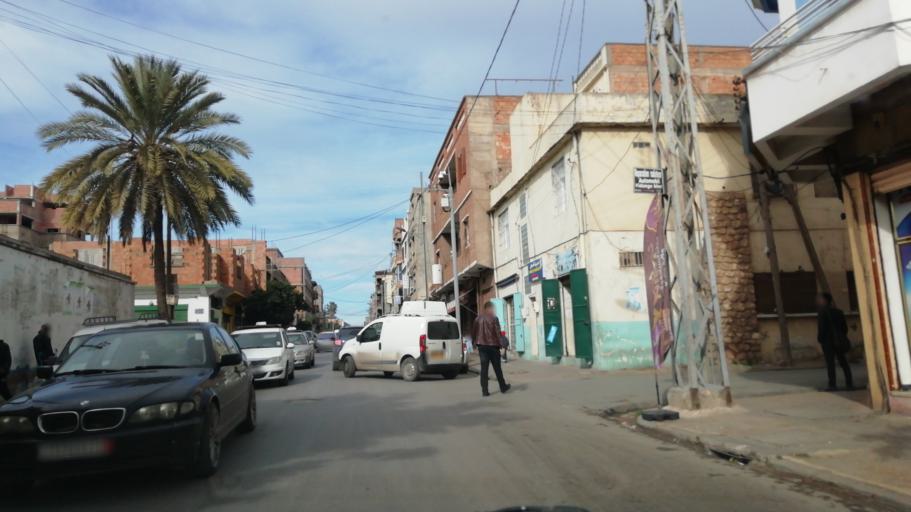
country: DZ
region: Oran
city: Oran
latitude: 35.6913
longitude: -0.6275
